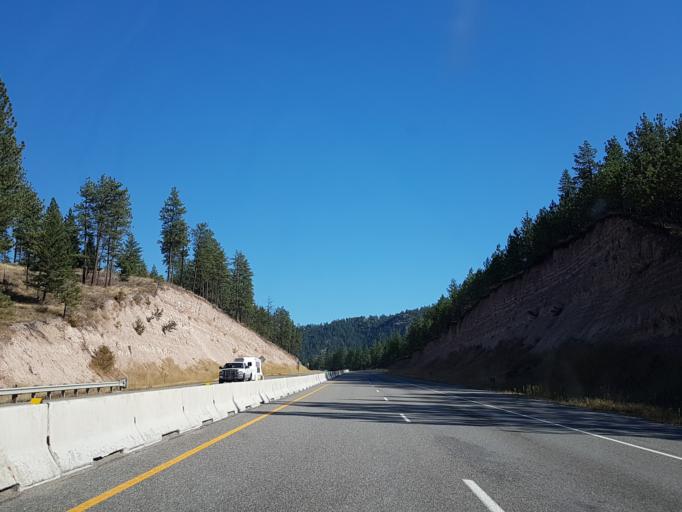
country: US
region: Montana
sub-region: Missoula County
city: Frenchtown
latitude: 47.0210
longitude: -114.3807
